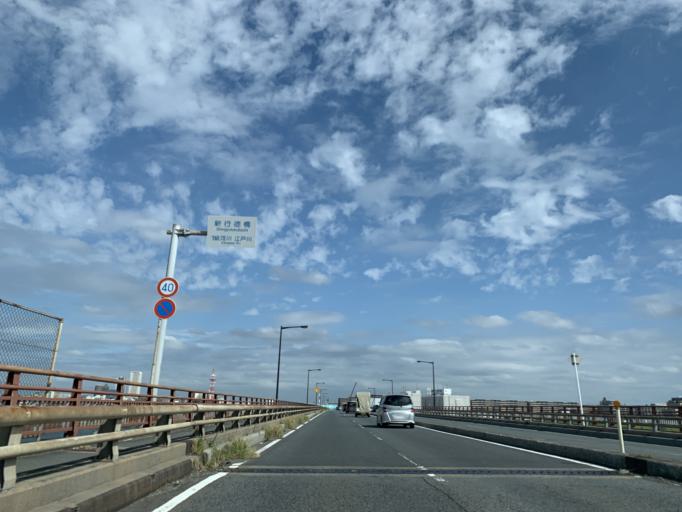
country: JP
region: Tokyo
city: Urayasu
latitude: 35.7004
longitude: 139.9245
